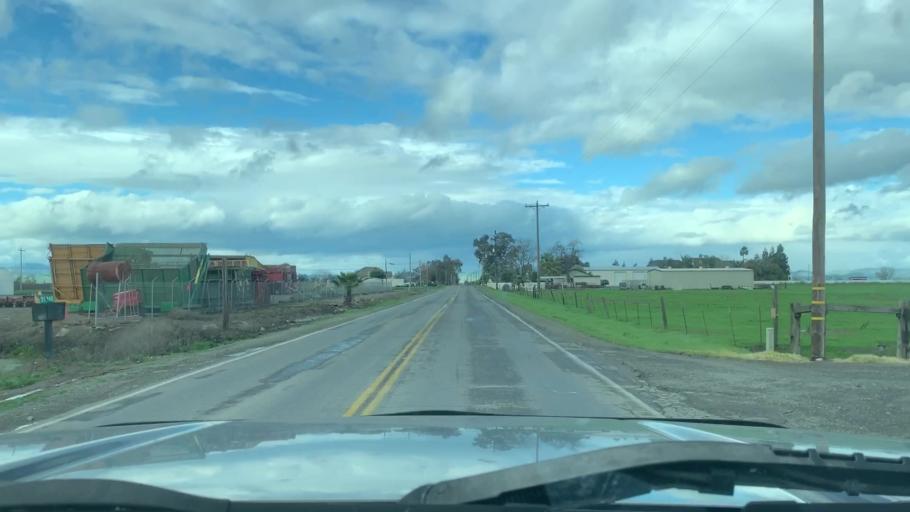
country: US
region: California
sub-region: Merced County
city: Los Banos
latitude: 37.1000
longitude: -120.8758
